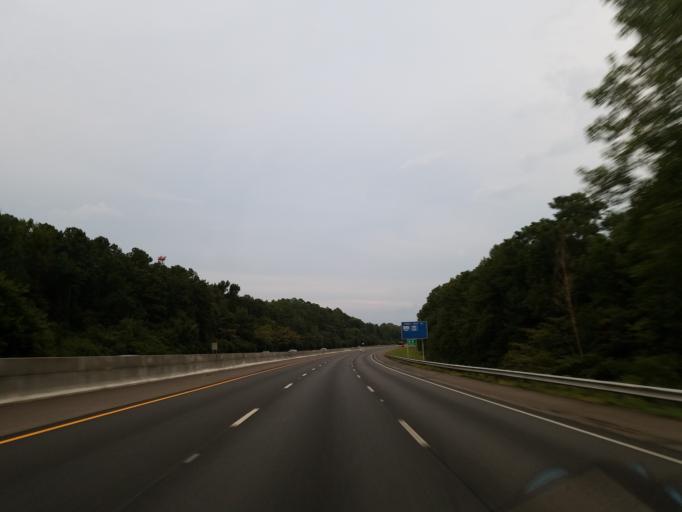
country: US
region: Alabama
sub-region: Tuscaloosa County
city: Lake View
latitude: 33.2450
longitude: -87.1465
